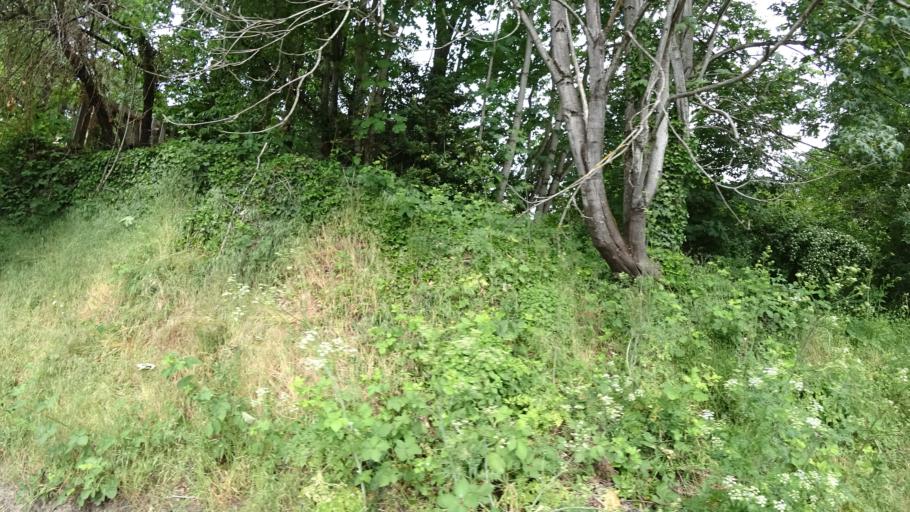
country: US
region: Oregon
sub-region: Washington County
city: West Haven
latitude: 45.5912
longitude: -122.7621
